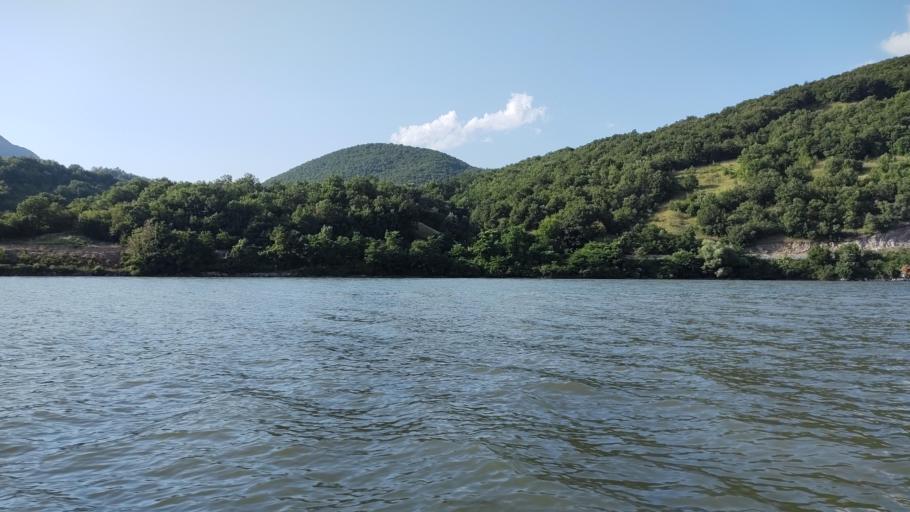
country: RO
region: Mehedinti
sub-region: Comuna Svinita
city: Svinita
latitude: 44.4797
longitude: 22.1633
